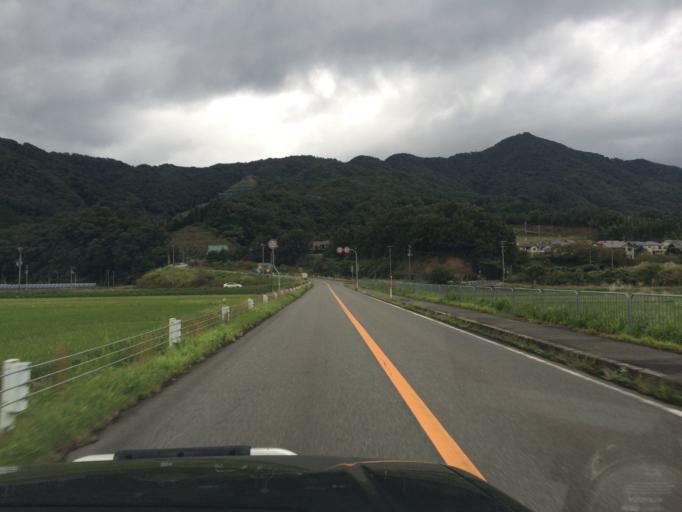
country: JP
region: Hyogo
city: Toyooka
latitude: 35.4364
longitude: 134.7945
